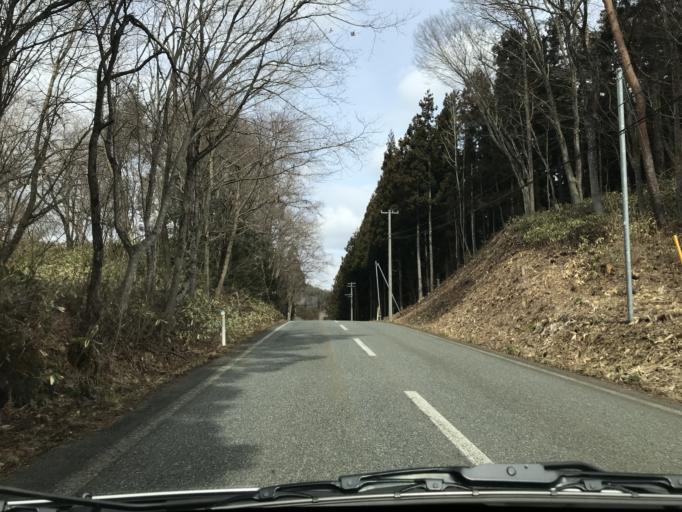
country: JP
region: Iwate
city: Kitakami
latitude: 39.2582
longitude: 141.3171
